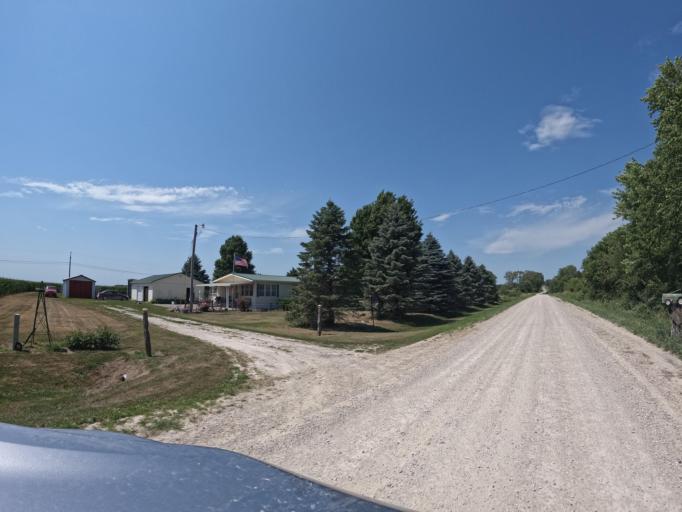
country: US
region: Iowa
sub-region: Henry County
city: Mount Pleasant
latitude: 40.9107
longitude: -91.6364
